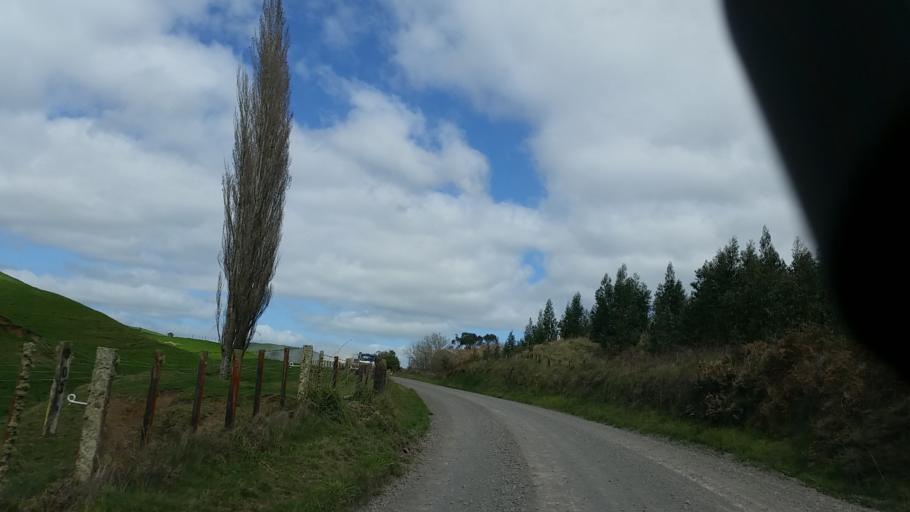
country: NZ
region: Bay of Plenty
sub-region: Rotorua District
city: Rotorua
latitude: -38.3628
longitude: 176.2083
